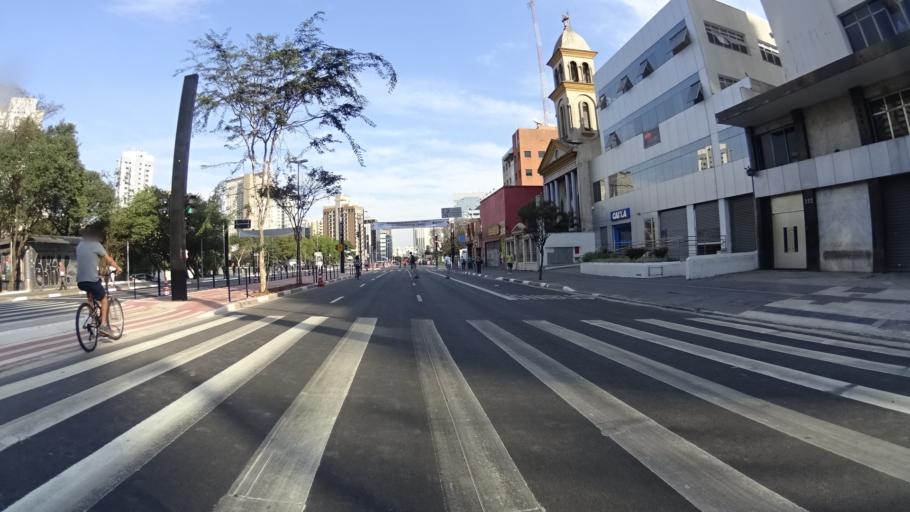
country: BR
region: Sao Paulo
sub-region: Sao Paulo
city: Sao Paulo
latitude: -23.5744
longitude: -46.6422
